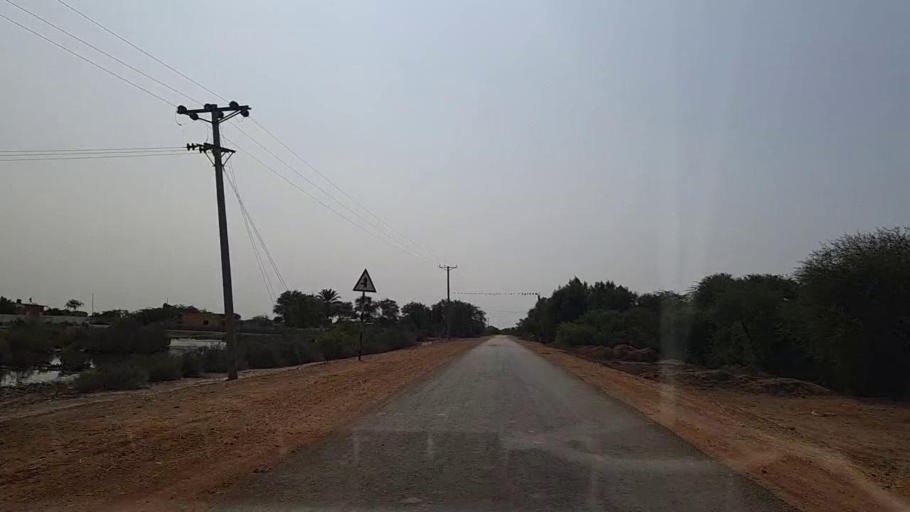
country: PK
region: Sindh
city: Chuhar Jamali
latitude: 24.3242
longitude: 67.9422
